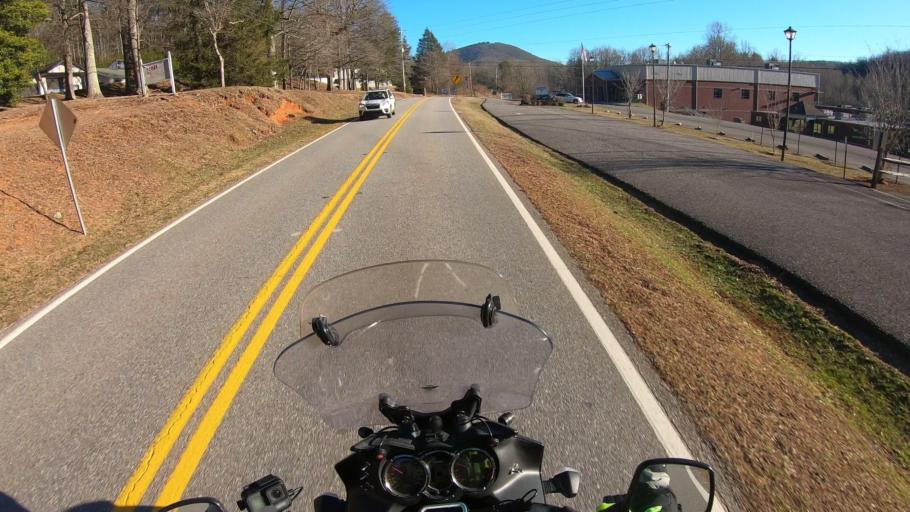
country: US
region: Georgia
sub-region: Lumpkin County
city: Dahlonega
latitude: 34.7046
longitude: -84.0370
